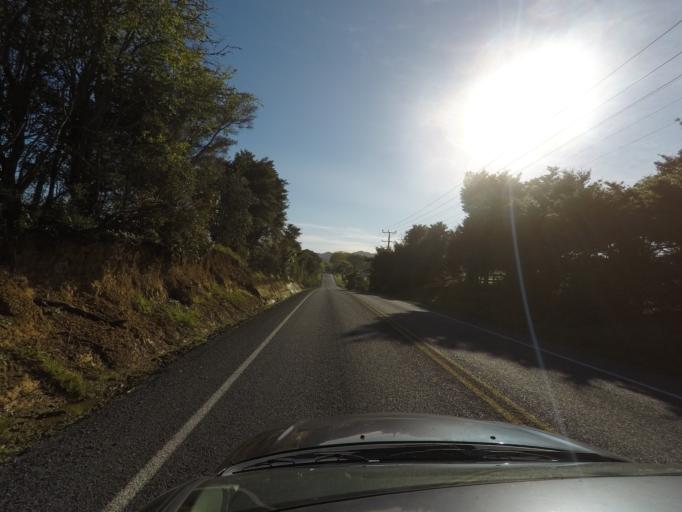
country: NZ
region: Auckland
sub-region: Auckland
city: Red Hill
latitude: -36.9914
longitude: 174.9871
